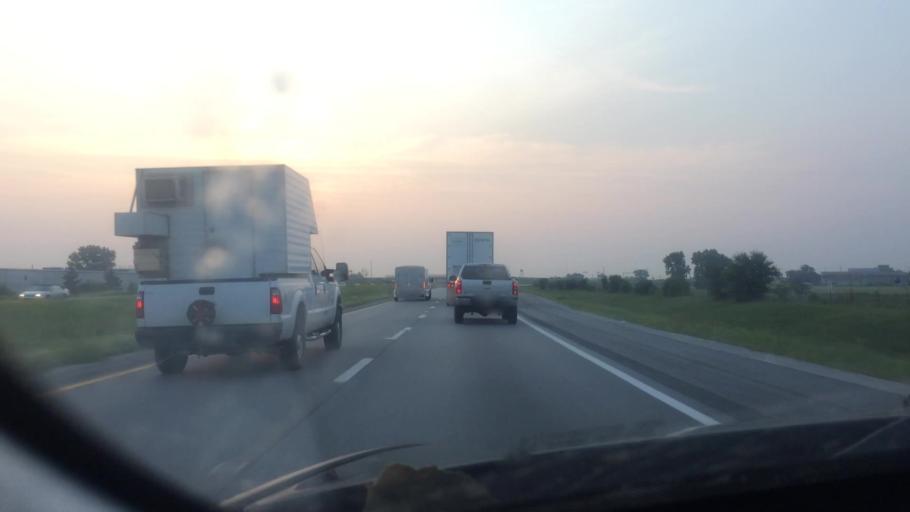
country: US
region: Ohio
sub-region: Wood County
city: Perrysburg
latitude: 41.5322
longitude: -83.6450
